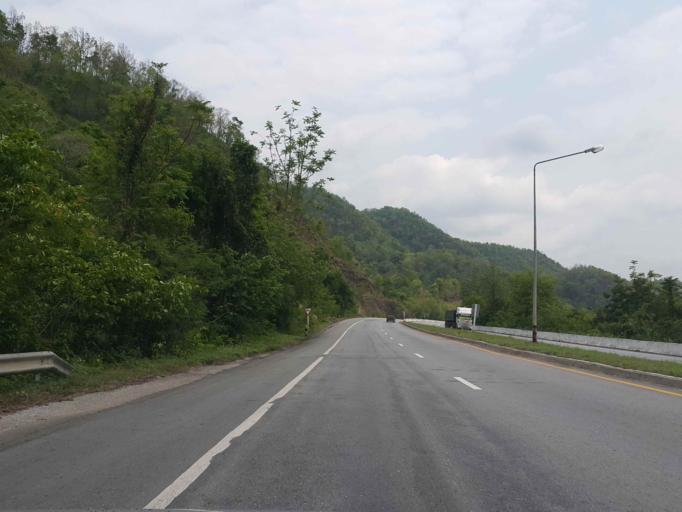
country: TH
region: Lampang
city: Sop Prap
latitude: 17.8446
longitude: 99.2932
